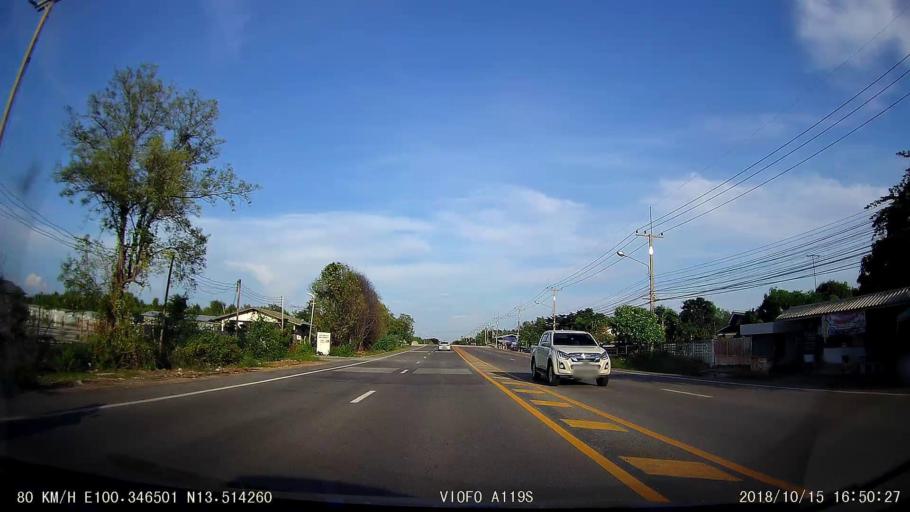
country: TH
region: Samut Sakhon
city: Samut Sakhon
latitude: 13.5143
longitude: 100.3467
